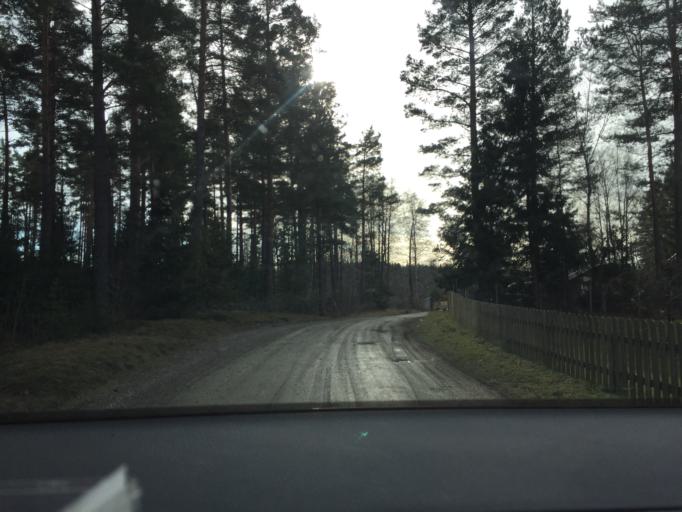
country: SE
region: OErebro
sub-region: Orebro Kommun
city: Odensbacken
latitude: 59.1276
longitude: 15.4742
